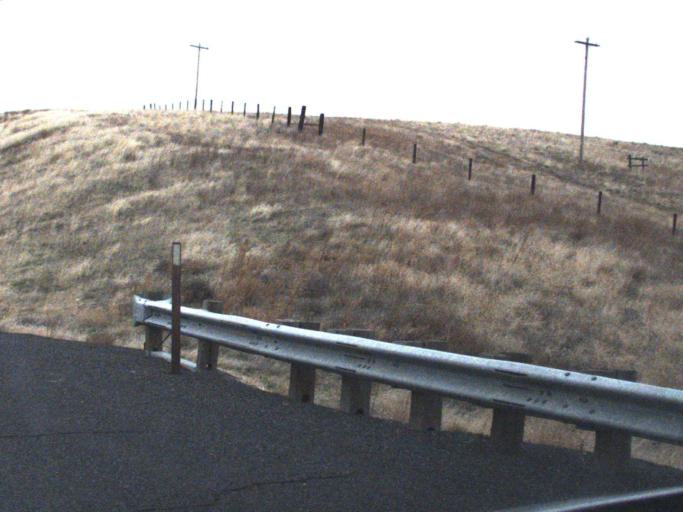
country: US
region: Washington
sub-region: Columbia County
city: Dayton
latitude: 46.7659
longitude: -118.0069
